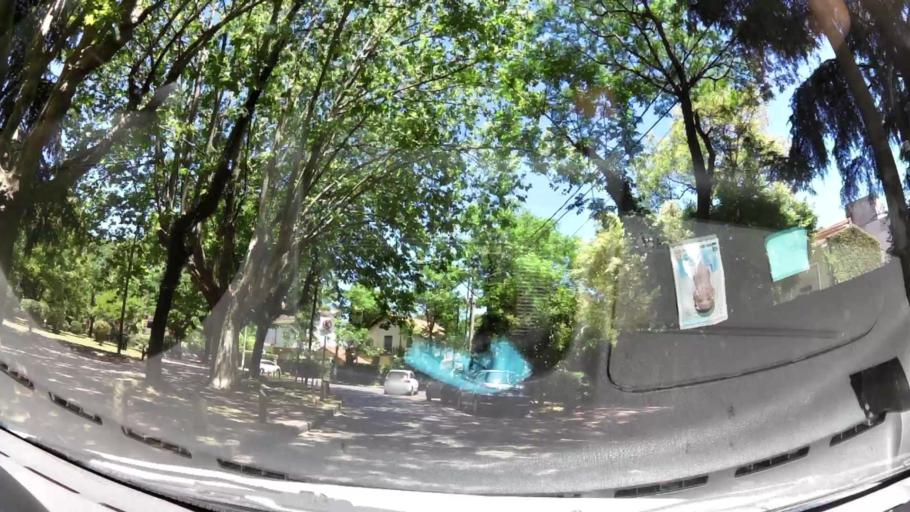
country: AR
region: Buenos Aires
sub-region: Partido de San Isidro
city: San Isidro
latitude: -34.4743
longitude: -58.5069
